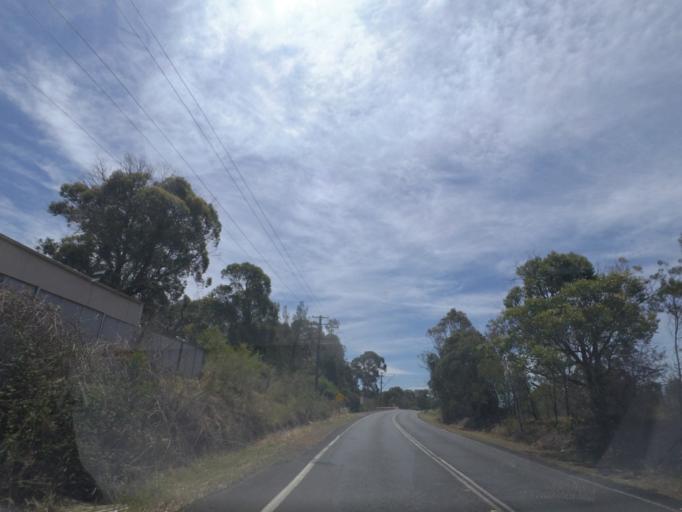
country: AU
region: New South Wales
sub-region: Wollondilly
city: Buxton
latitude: -34.2779
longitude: 150.5772
